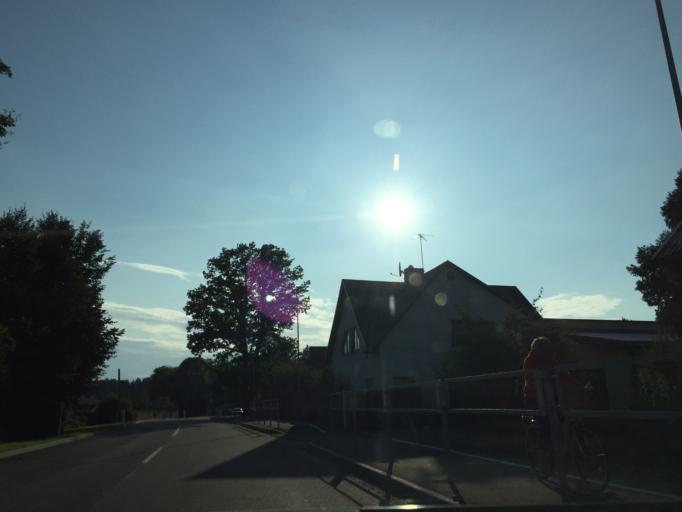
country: LV
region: Ogre
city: Ogre
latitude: 56.8134
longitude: 24.6437
